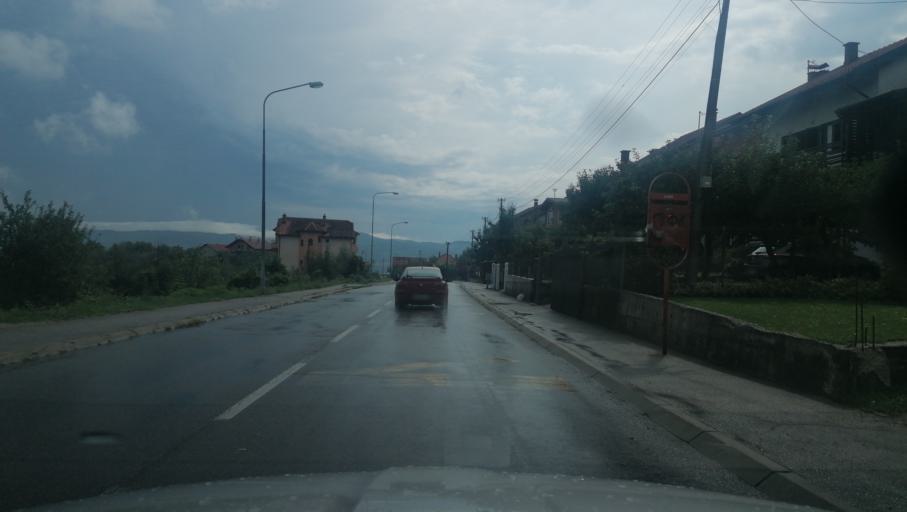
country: BA
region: Republika Srpska
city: Banja Luka
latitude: 44.7902
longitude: 17.1804
